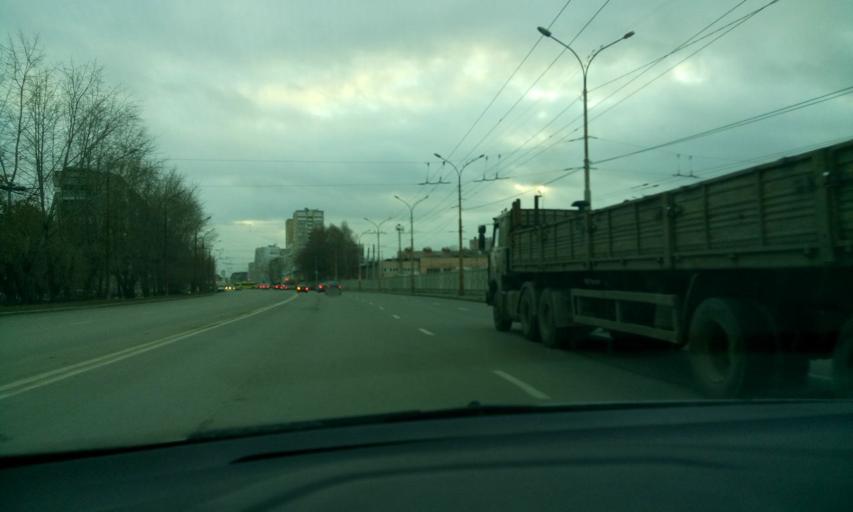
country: RU
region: Sverdlovsk
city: Verkhnyaya Pyshma
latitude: 56.9119
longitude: 60.5964
